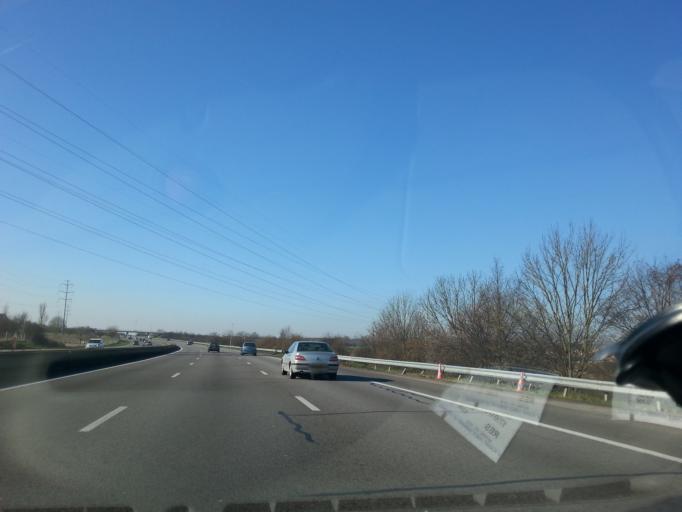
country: FR
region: Ile-de-France
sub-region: Departement des Yvelines
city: Bouafle
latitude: 48.9696
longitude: 1.9144
